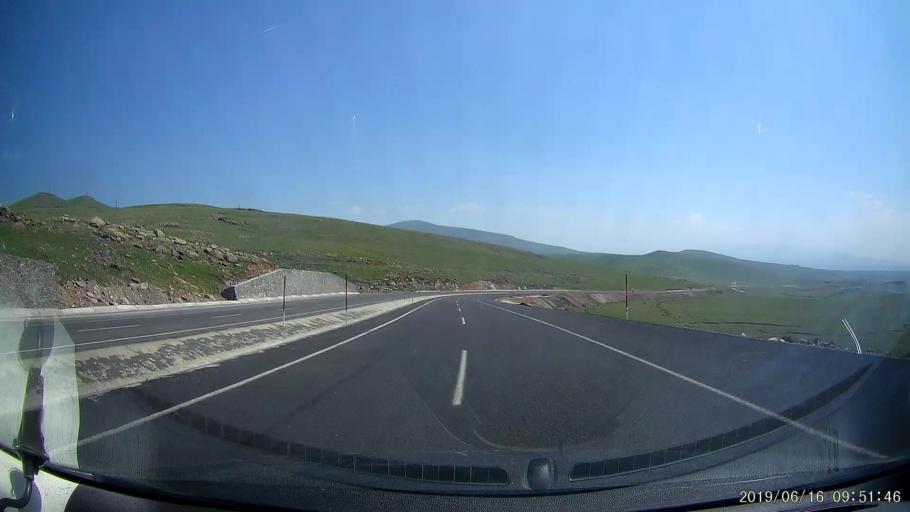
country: TR
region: Kars
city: Digor
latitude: 40.3913
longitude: 43.3727
